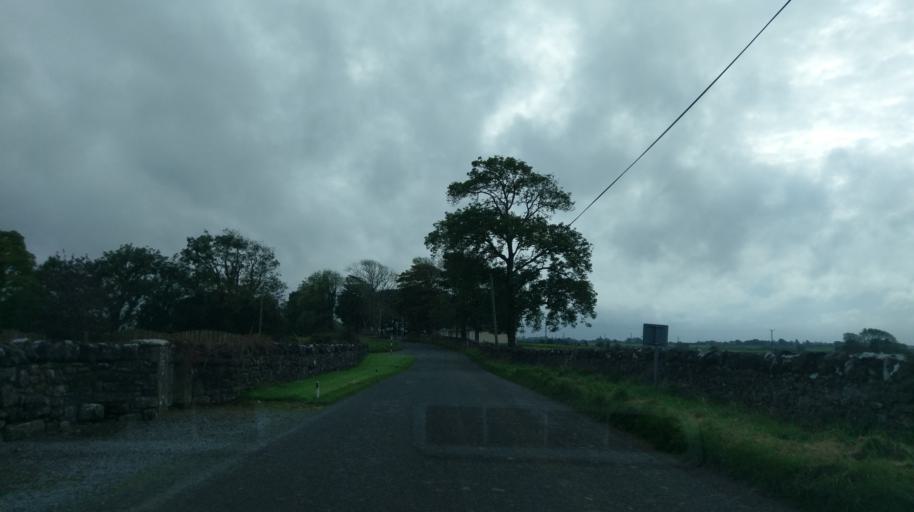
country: IE
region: Connaught
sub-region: County Galway
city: Athenry
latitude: 53.4538
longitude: -8.5861
